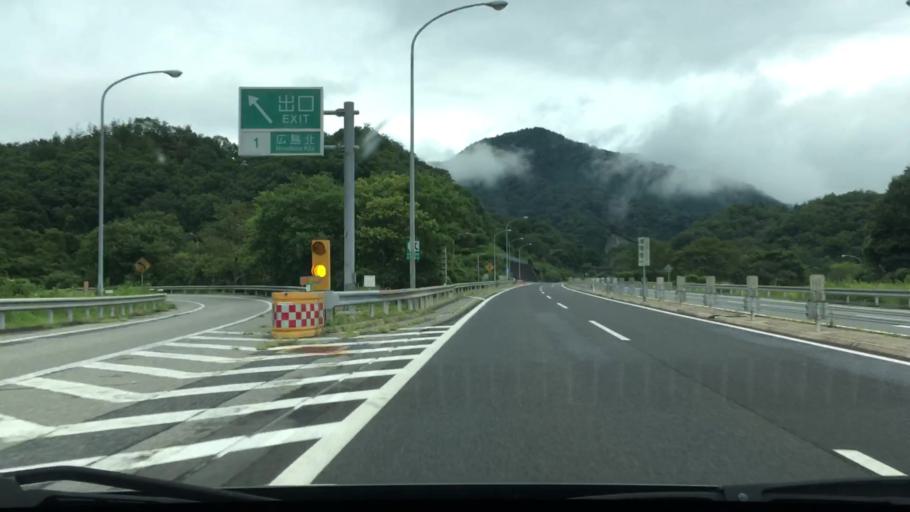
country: JP
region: Hiroshima
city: Hiroshima-shi
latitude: 34.5520
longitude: 132.4517
